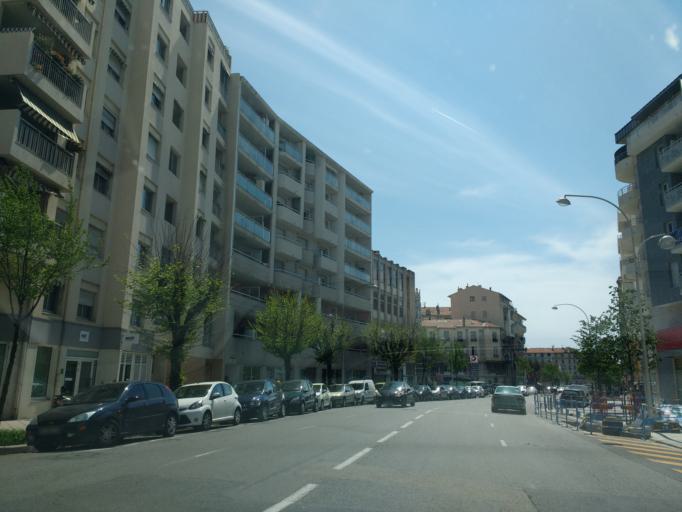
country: FR
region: Provence-Alpes-Cote d'Azur
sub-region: Departement des Alpes-Maritimes
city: Villefranche-sur-Mer
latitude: 43.7077
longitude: 7.2927
